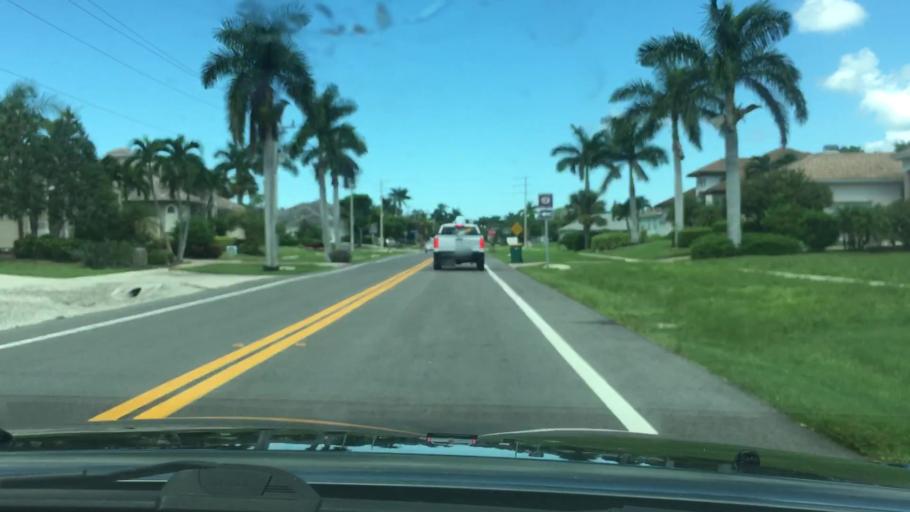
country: US
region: Florida
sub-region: Collier County
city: Marco
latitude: 25.9516
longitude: -81.7387
